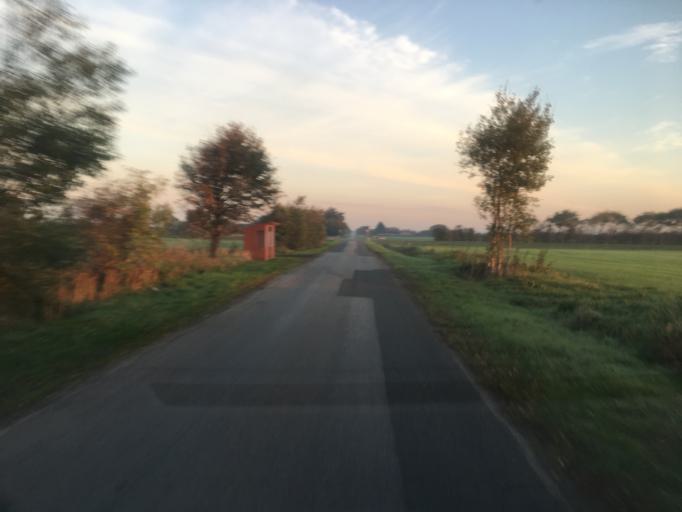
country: DK
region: South Denmark
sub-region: Tonder Kommune
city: Logumkloster
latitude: 55.0614
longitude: 9.0235
